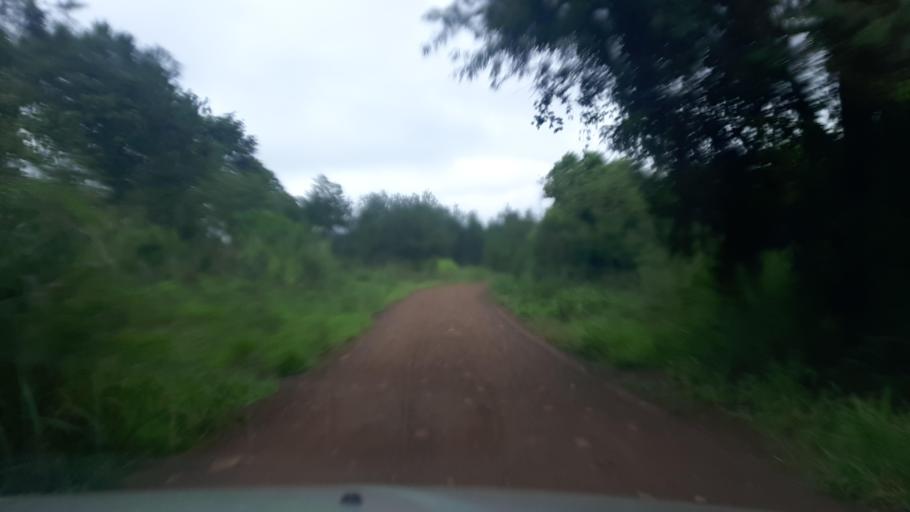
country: BR
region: Parana
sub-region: Ampere
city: Ampere
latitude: -26.0516
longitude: -53.5547
